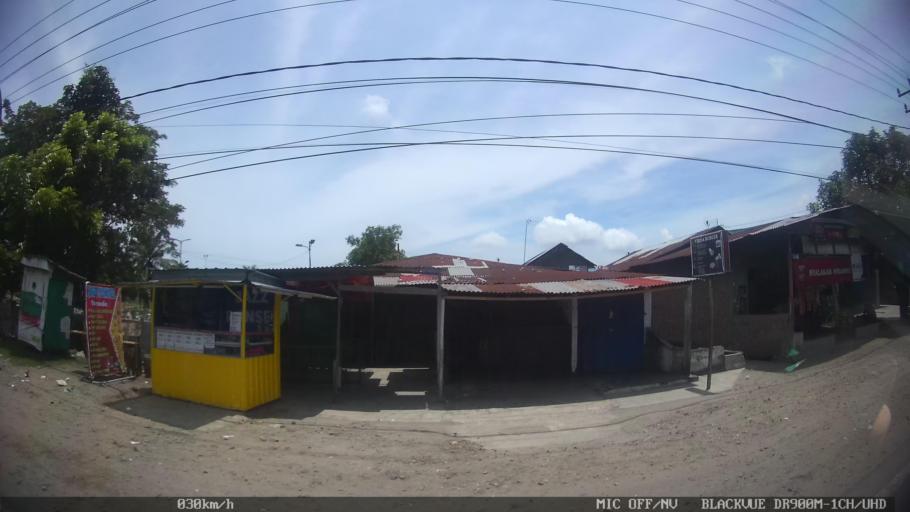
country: ID
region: North Sumatra
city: Labuhan Deli
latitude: 3.7449
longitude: 98.6746
